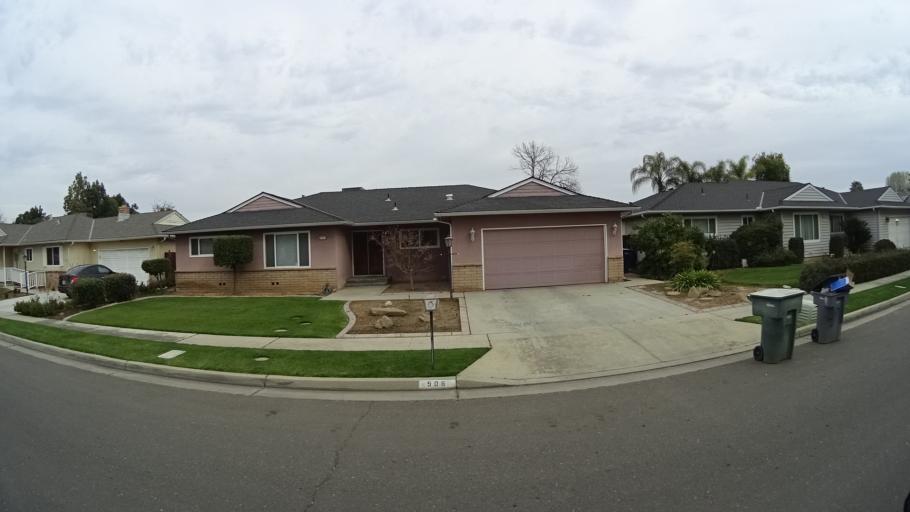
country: US
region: California
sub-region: Fresno County
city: Clovis
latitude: 36.8393
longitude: -119.7678
